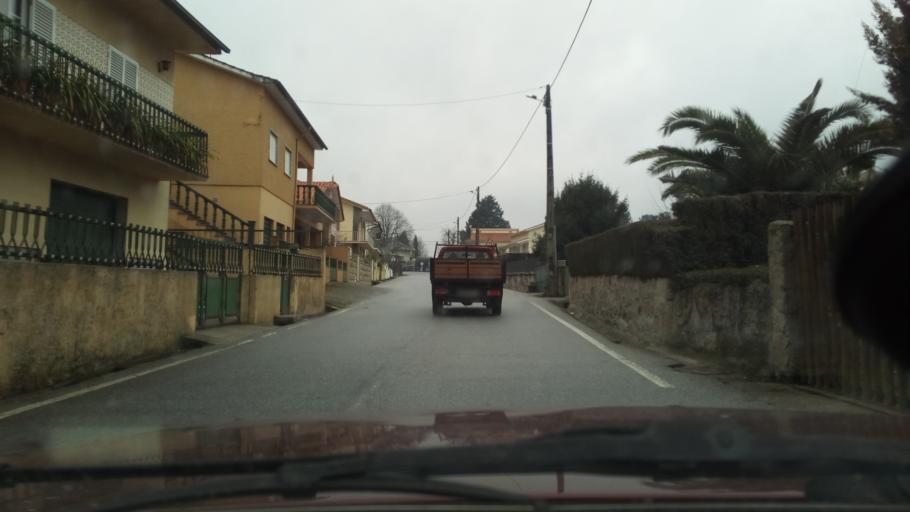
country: PT
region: Viseu
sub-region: Mangualde
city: Mangualde
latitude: 40.6053
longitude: -7.8197
